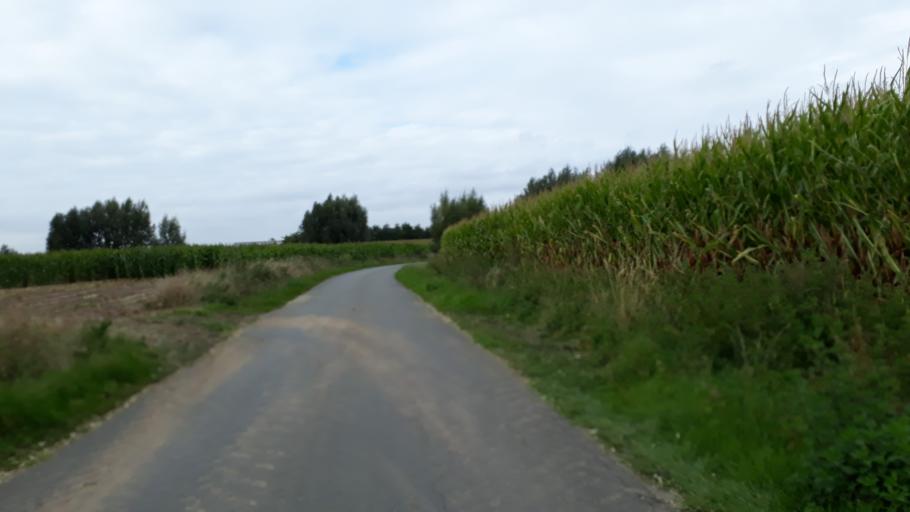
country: BE
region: Flanders
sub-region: Provincie West-Vlaanderen
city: Torhout
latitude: 51.0430
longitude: 3.1170
